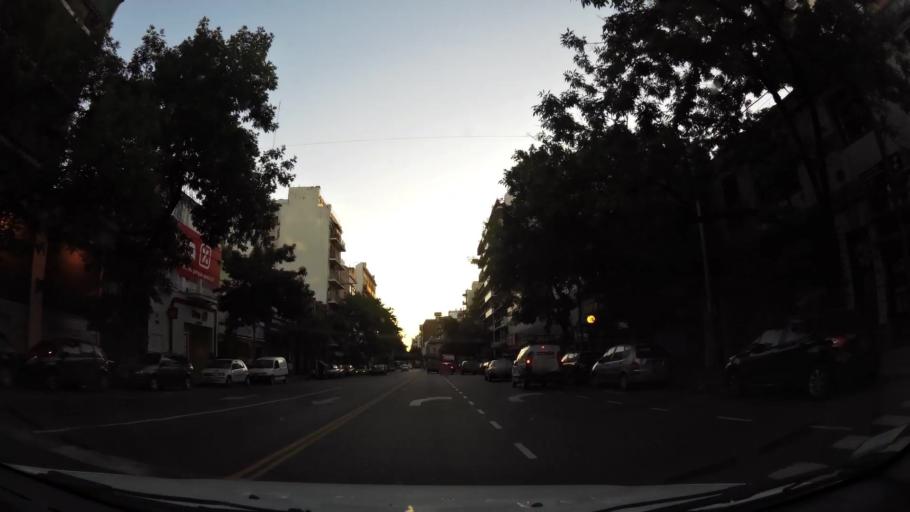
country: AR
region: Buenos Aires F.D.
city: Colegiales
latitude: -34.6014
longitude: -58.4413
